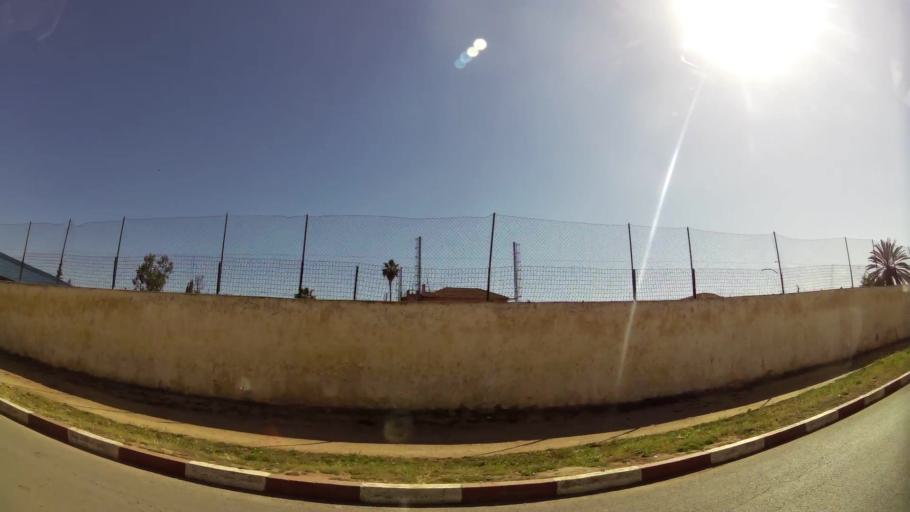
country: MA
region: Meknes-Tafilalet
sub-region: Meknes
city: Meknes
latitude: 33.8884
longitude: -5.5311
